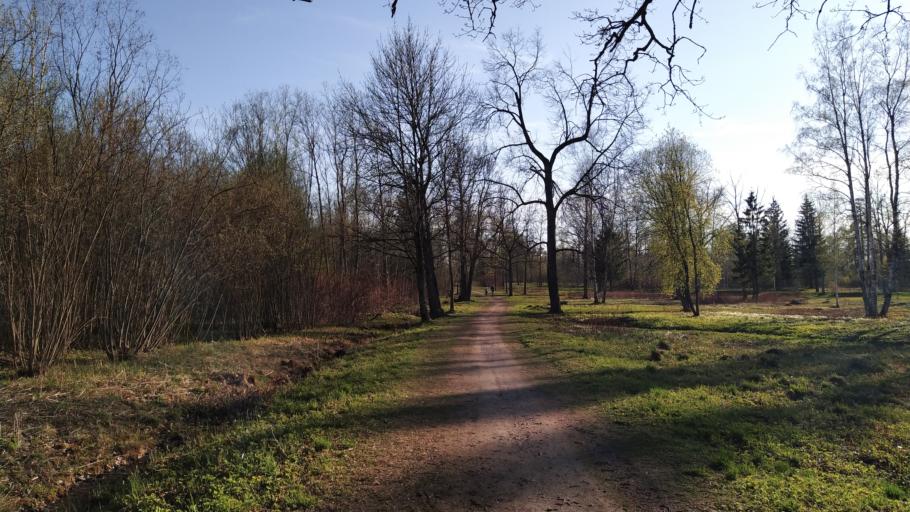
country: RU
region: St.-Petersburg
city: Aleksandrovskaya
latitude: 59.7077
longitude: 30.3510
